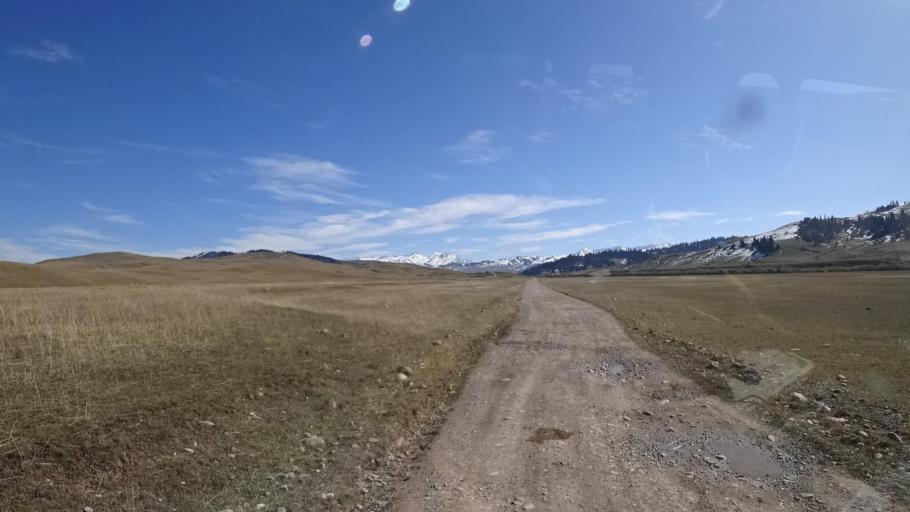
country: KZ
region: Almaty Oblysy
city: Kegen
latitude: 42.7435
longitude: 78.9983
